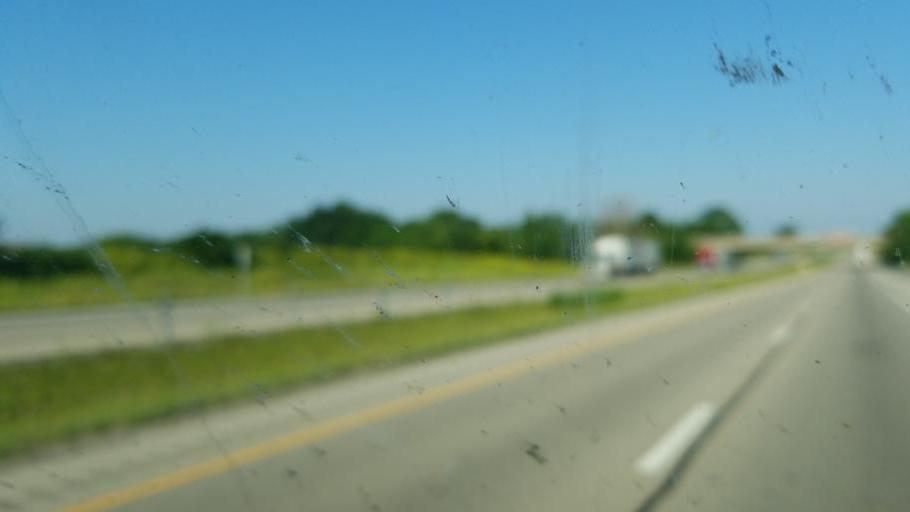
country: US
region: Illinois
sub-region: LaSalle County
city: Marseilles
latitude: 41.3755
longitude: -88.6881
